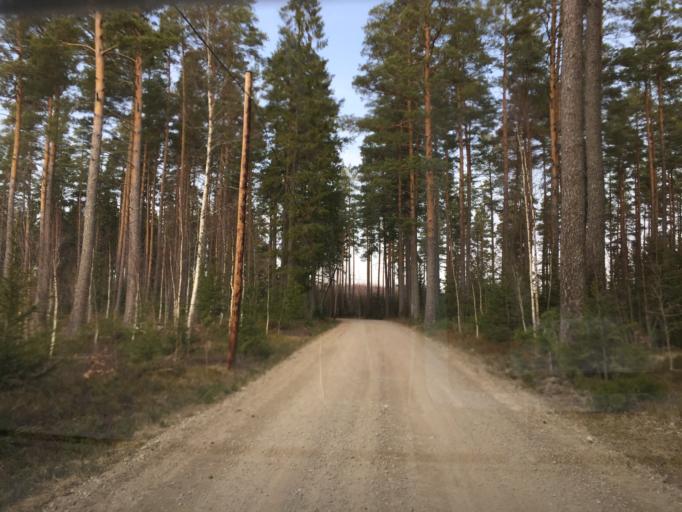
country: SE
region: Soedermanland
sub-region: Vingakers Kommun
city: Vingaker
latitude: 59.0267
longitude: 15.7783
